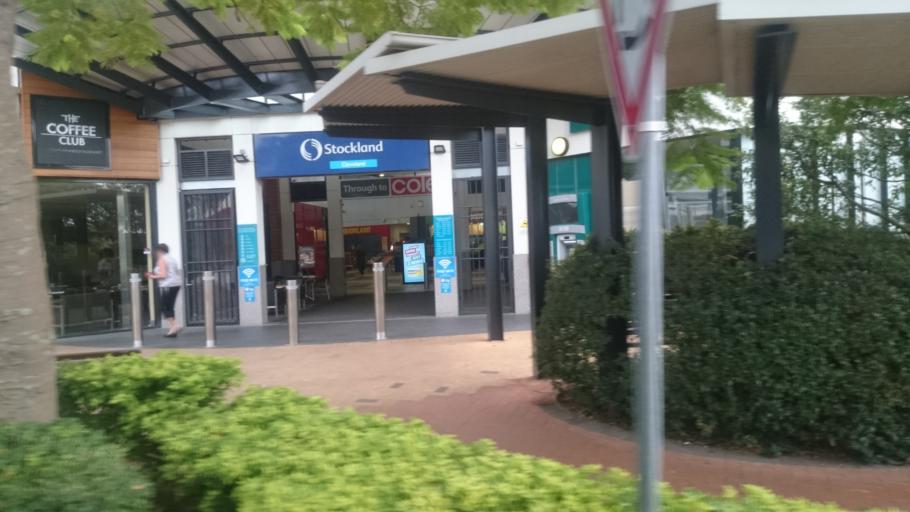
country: AU
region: Queensland
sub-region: Redland
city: Cleveland
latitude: -27.5259
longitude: 153.2692
